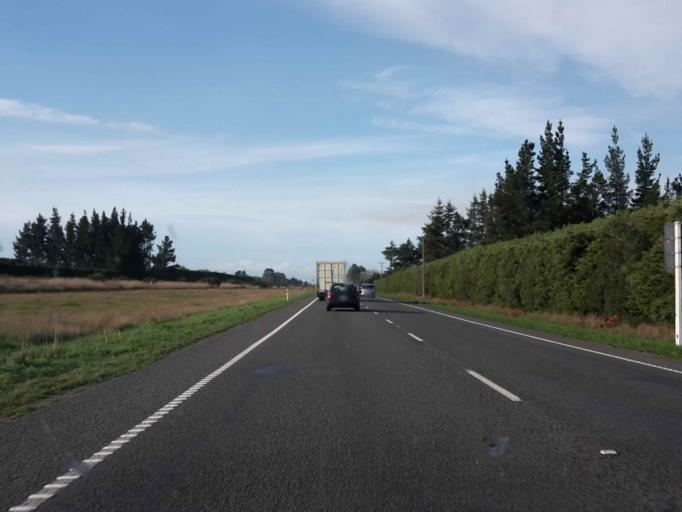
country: NZ
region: Canterbury
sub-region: Ashburton District
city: Tinwald
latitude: -43.9370
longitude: 171.6890
